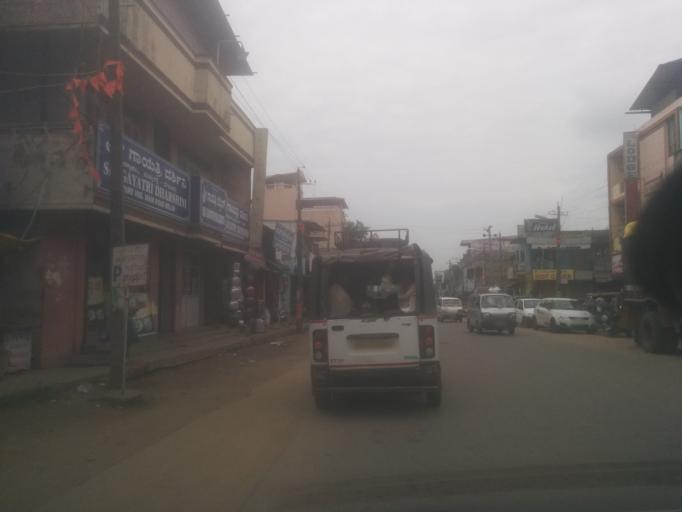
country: IN
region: Karnataka
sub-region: Hassan
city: Belur
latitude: 13.1664
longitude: 75.8675
